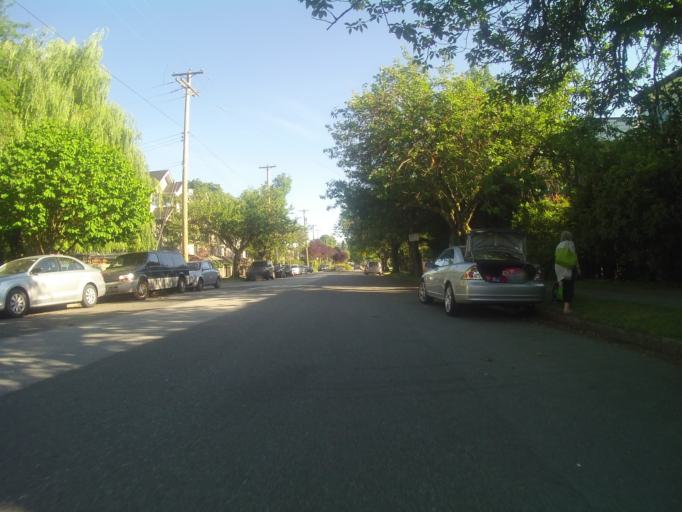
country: CA
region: British Columbia
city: Vancouver
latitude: 49.2559
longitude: -123.1202
